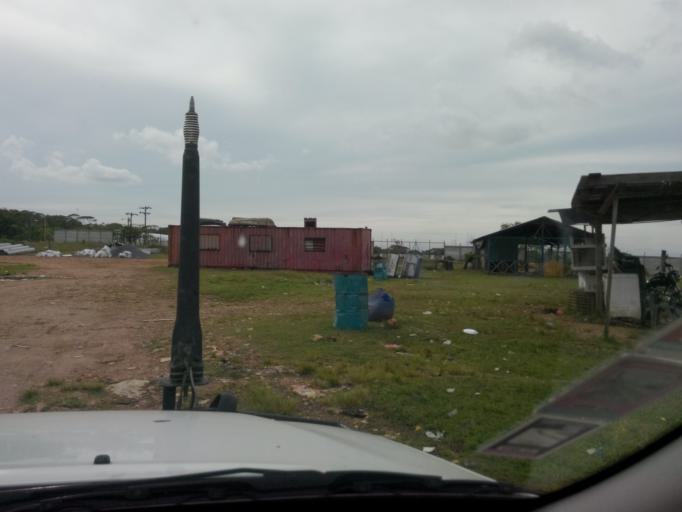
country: NI
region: Atlantico Sur
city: Bluefields
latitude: 12.0339
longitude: -83.7636
